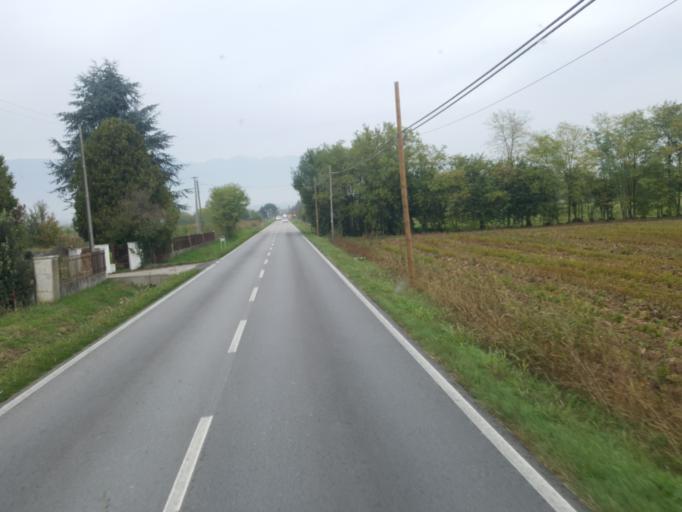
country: IT
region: Veneto
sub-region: Provincia di Treviso
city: Loria Bessica
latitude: 45.7457
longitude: 11.8659
